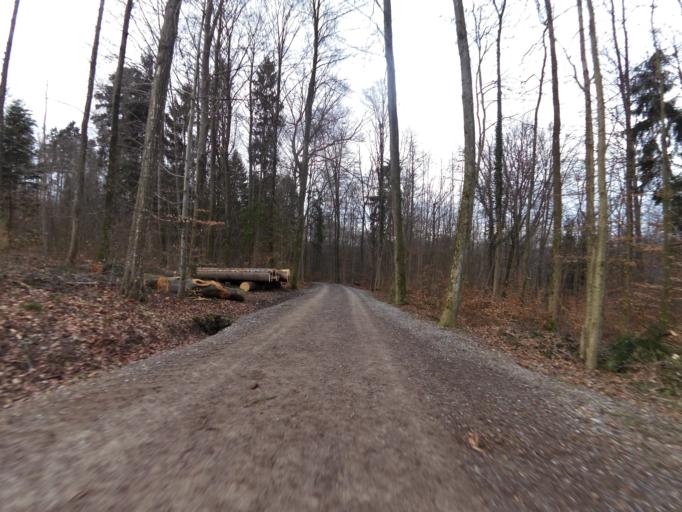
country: CH
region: Zurich
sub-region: Bezirk Dietikon
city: Schlieren / Boden
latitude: 47.3889
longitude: 8.4596
